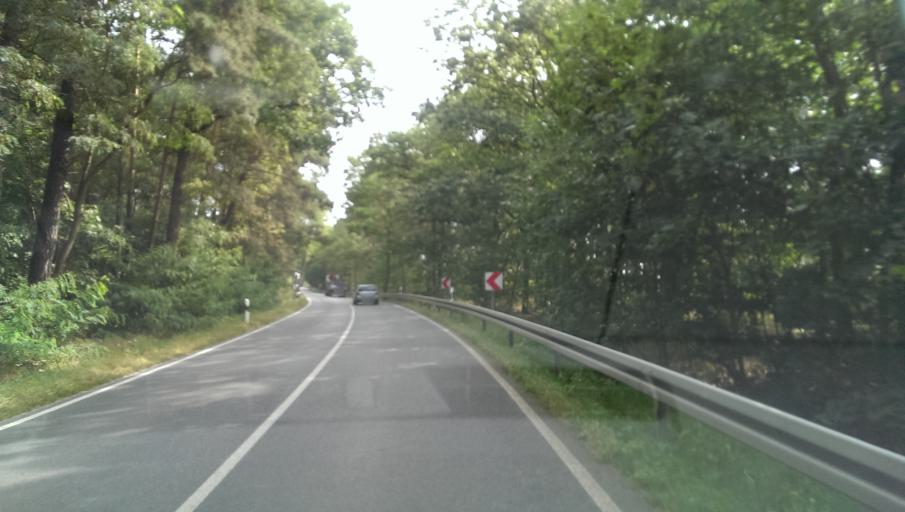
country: DE
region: Brandenburg
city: Am Mellensee
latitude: 52.2252
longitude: 13.3760
